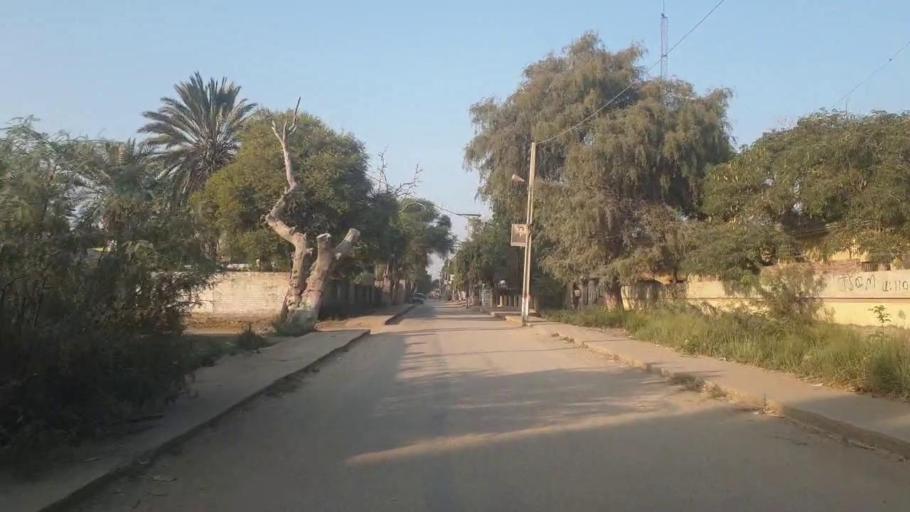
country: PK
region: Sindh
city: Jamshoro
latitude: 25.4405
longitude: 68.2959
